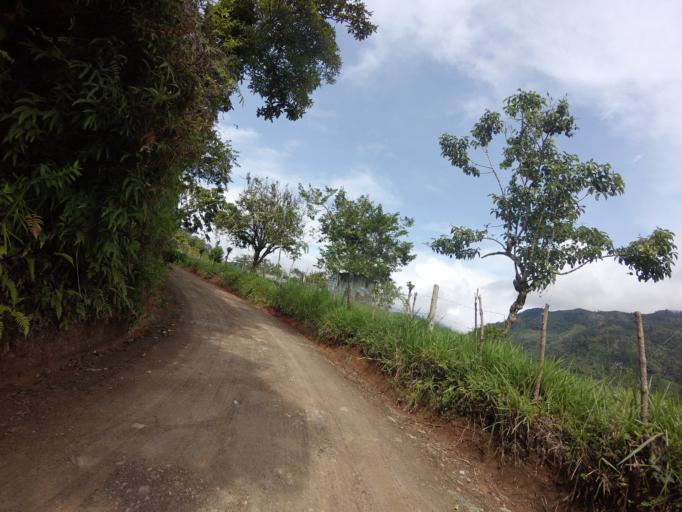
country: CO
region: Caldas
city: Marquetalia
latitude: 5.3356
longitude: -75.0431
